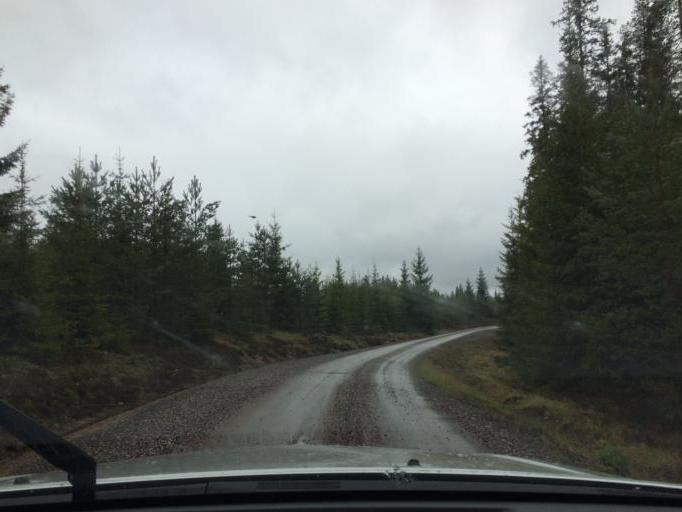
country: SE
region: OErebro
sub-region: Hallefors Kommun
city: Haellefors
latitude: 60.0256
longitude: 14.5591
